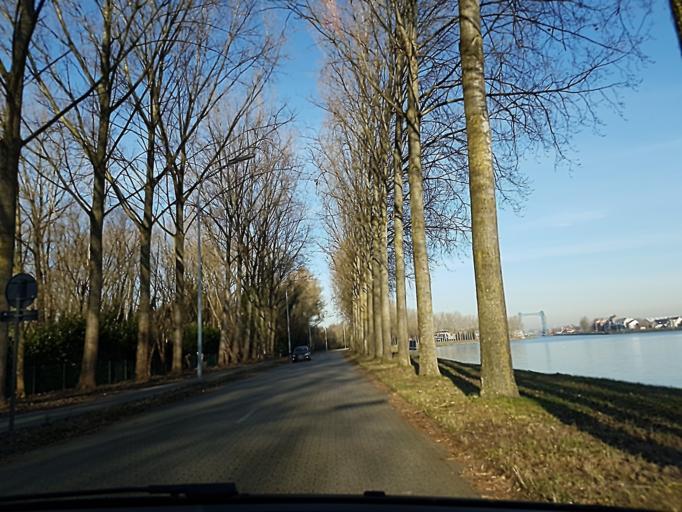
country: BE
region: Flanders
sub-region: Provincie Antwerpen
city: Willebroek
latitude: 51.0495
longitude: 4.3611
